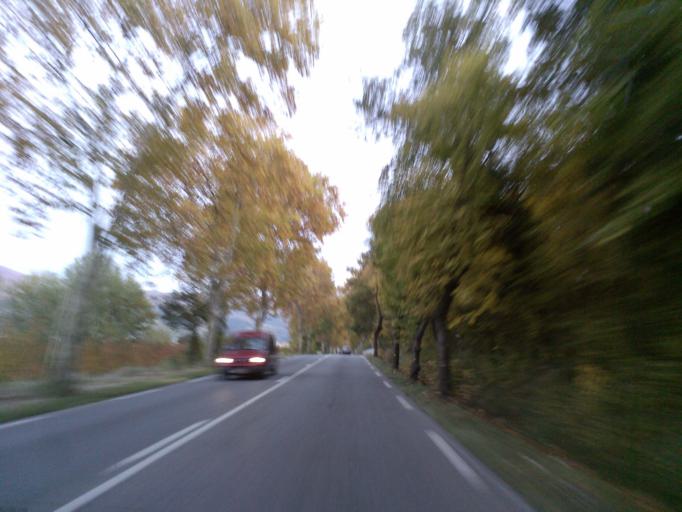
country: FR
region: Provence-Alpes-Cote d'Azur
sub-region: Departement des Alpes-de-Haute-Provence
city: Volonne
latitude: 44.1168
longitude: 5.9924
